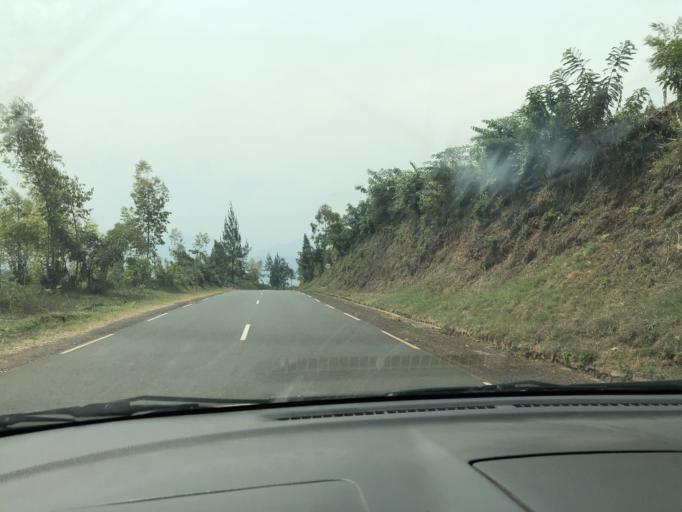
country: RW
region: Western Province
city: Cyangugu
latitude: -2.6690
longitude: 28.9965
